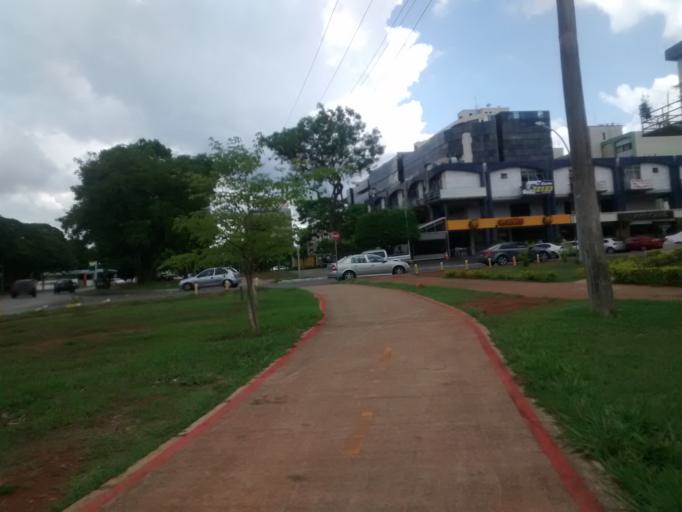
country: BR
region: Federal District
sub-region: Brasilia
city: Brasilia
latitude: -15.7569
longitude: -47.8823
